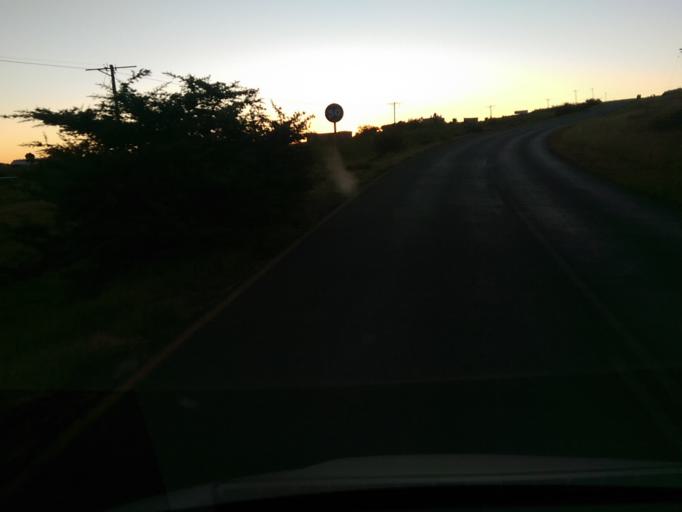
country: LS
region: Maseru
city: Nako
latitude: -29.4365
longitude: 27.6848
